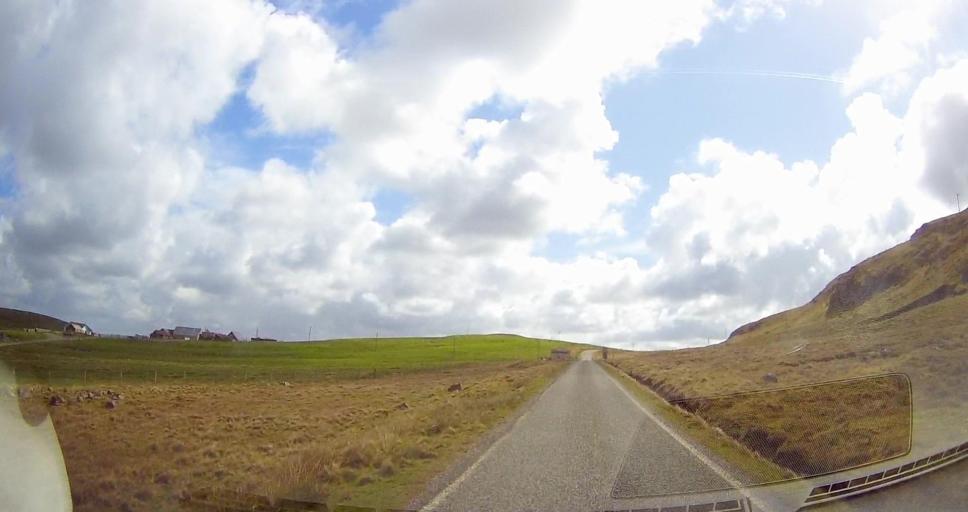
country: GB
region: Scotland
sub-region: Shetland Islands
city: Lerwick
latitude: 60.5465
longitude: -1.3403
